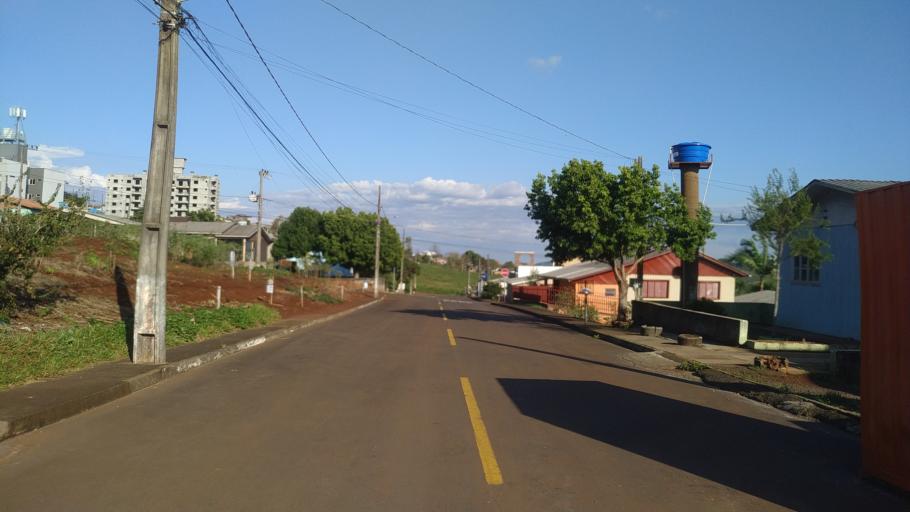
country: BR
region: Santa Catarina
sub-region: Chapeco
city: Chapeco
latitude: -27.0690
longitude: -52.6099
